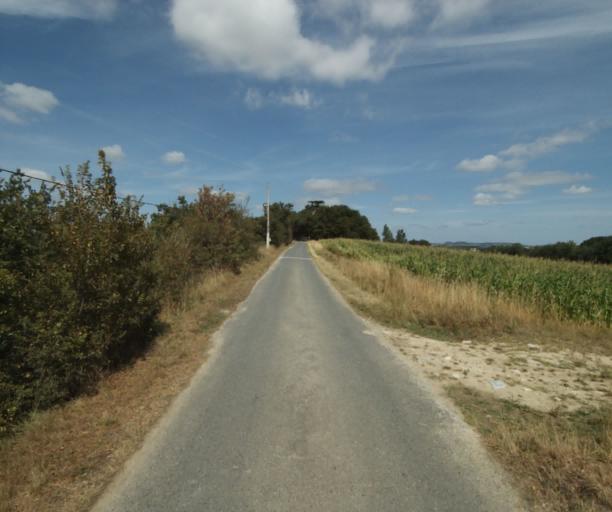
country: FR
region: Midi-Pyrenees
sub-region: Departement du Tarn
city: Dourgne
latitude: 43.4816
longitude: 2.1060
